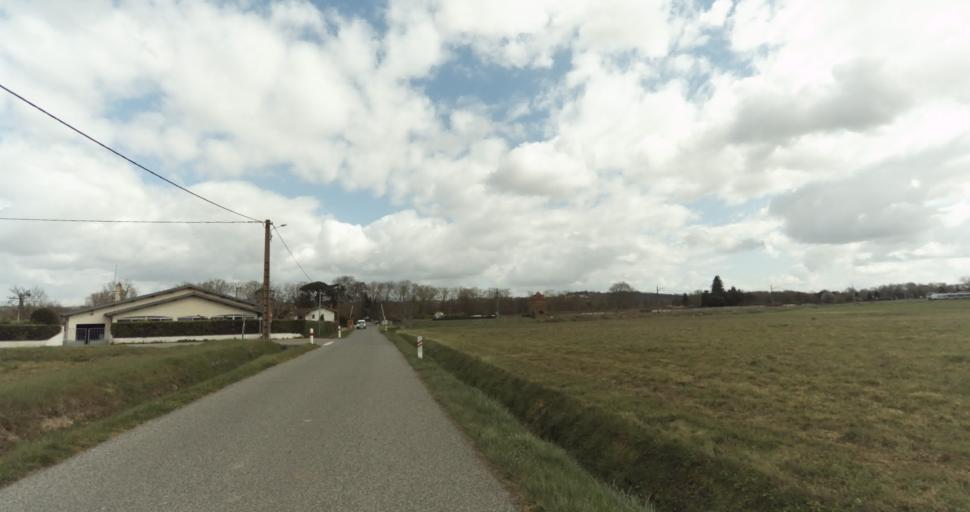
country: FR
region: Midi-Pyrenees
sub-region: Departement de la Haute-Garonne
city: Auterive
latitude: 43.3407
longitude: 1.4735
